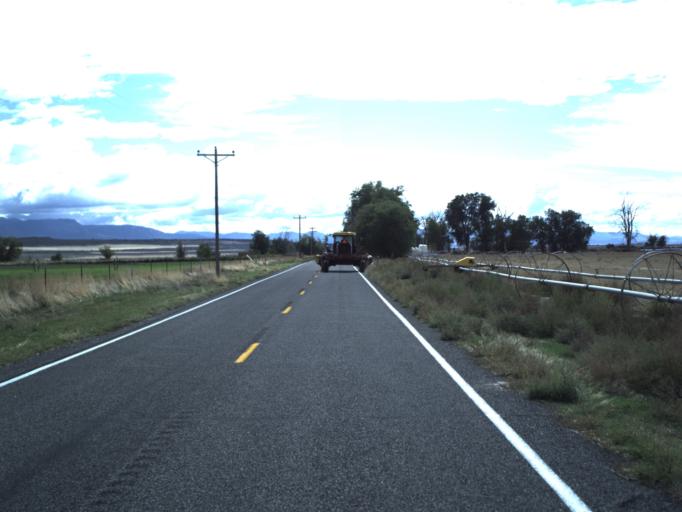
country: US
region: Utah
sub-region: Millard County
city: Fillmore
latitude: 39.0508
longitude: -112.4098
